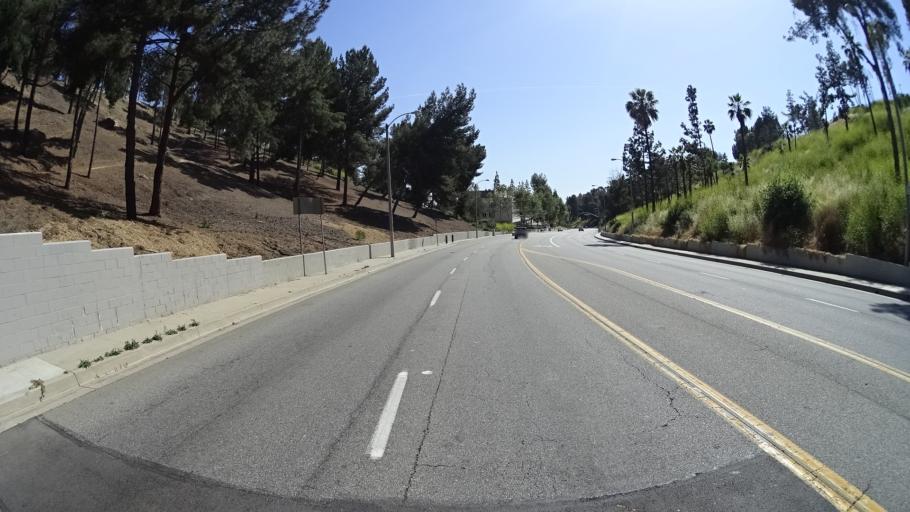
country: US
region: California
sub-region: Los Angeles County
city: Belvedere
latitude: 34.0524
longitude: -118.1734
